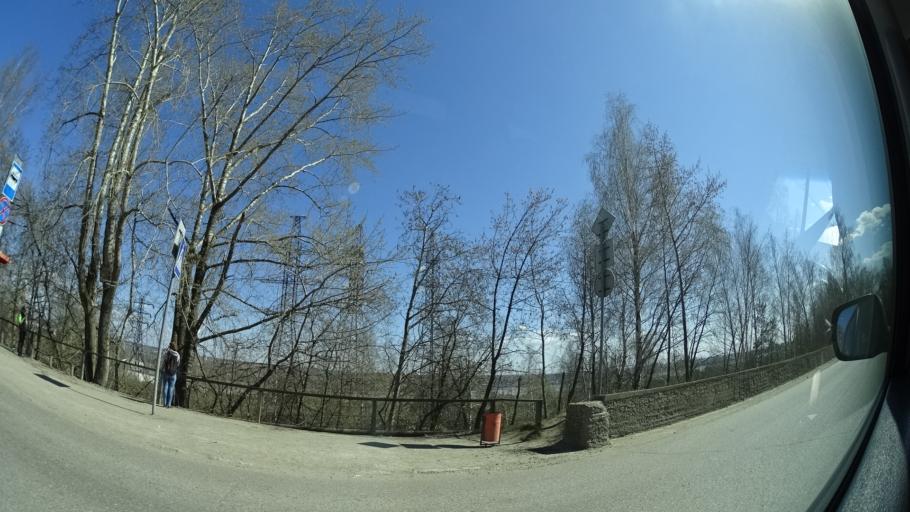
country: RU
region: Perm
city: Perm
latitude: 58.1137
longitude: 56.3198
